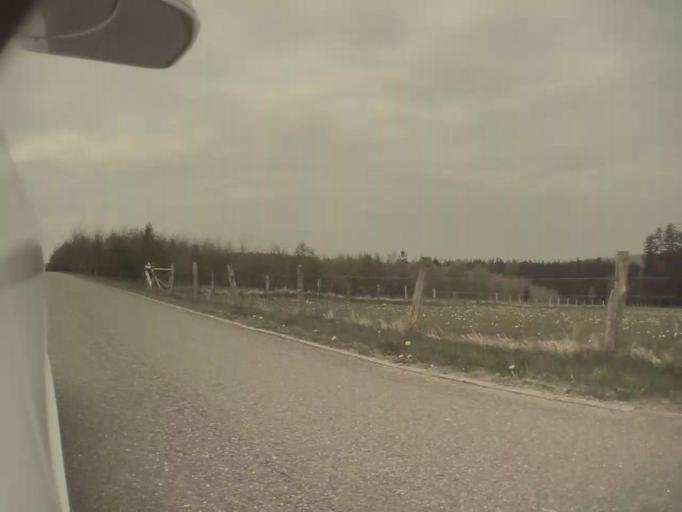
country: BE
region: Wallonia
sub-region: Province du Luxembourg
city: La Roche-en-Ardenne
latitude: 50.2276
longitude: 5.6105
